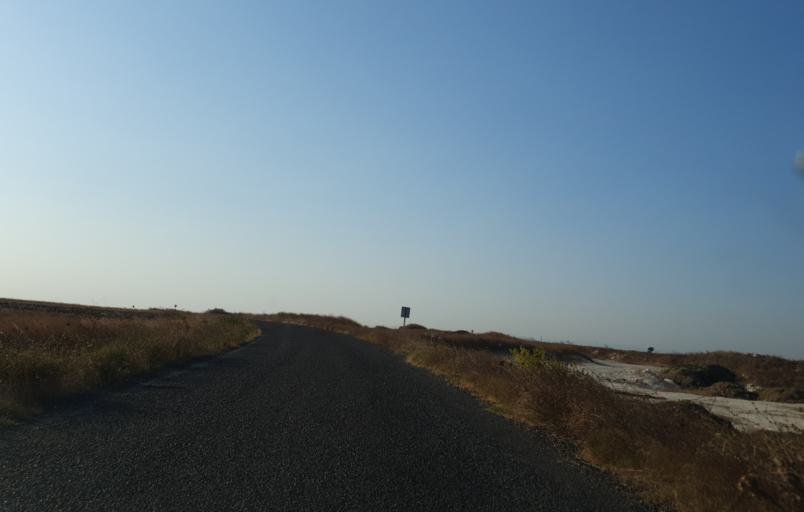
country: TR
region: Tekirdag
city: Beyazkoy
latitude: 41.4193
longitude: 27.7640
